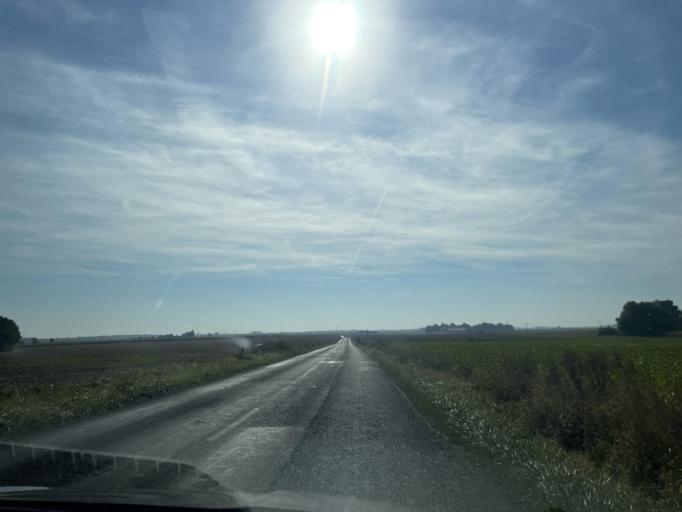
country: FR
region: Ile-de-France
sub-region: Departement de Seine-et-Marne
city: Sammeron
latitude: 48.8873
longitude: 3.0675
